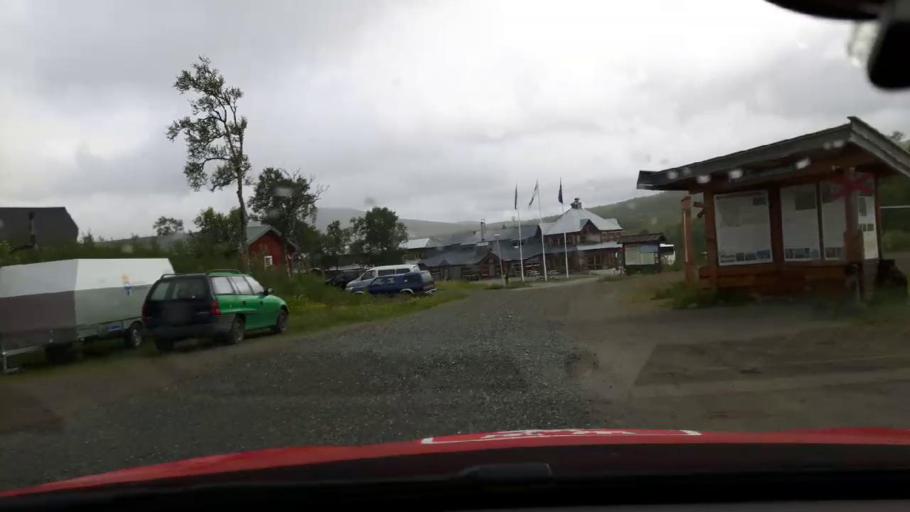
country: NO
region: Nord-Trondelag
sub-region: Meraker
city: Meraker
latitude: 63.1703
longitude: 12.3630
